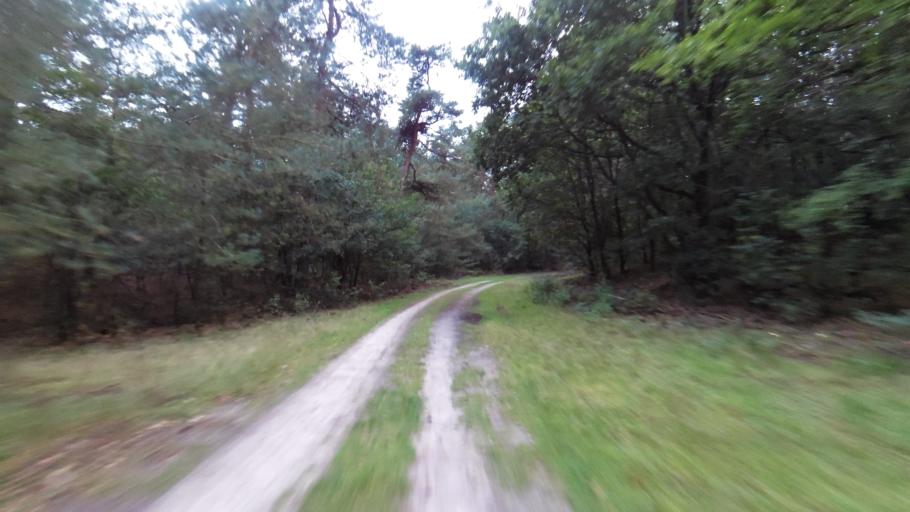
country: NL
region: Gelderland
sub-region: Gemeente Ede
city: Harskamp
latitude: 52.1796
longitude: 5.7771
